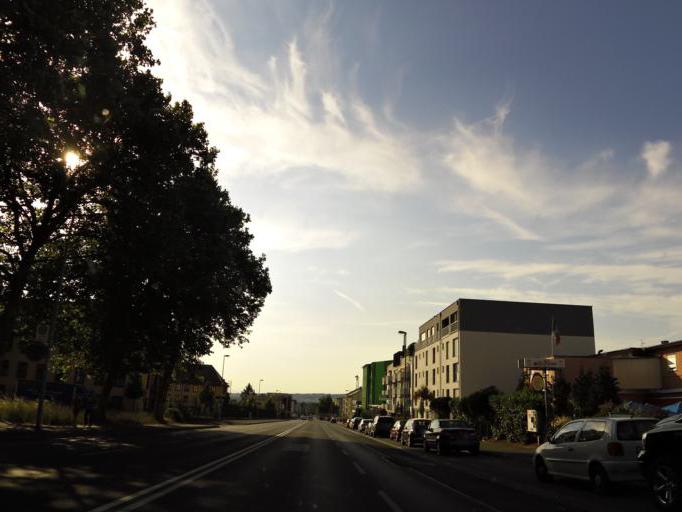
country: DE
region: Bavaria
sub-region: Regierungsbezirk Unterfranken
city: Aschaffenburg
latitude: 49.9669
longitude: 9.1684
